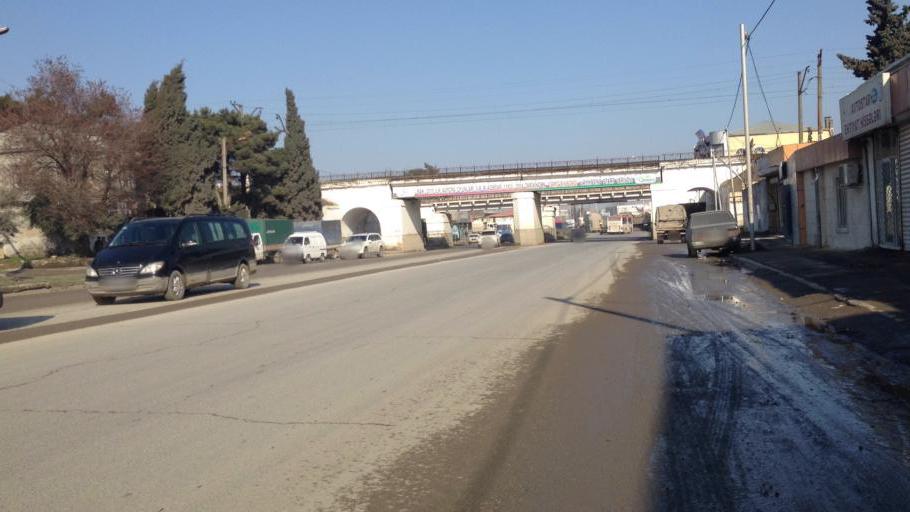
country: AZ
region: Baki
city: Binagadi
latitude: 40.4387
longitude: 49.8448
